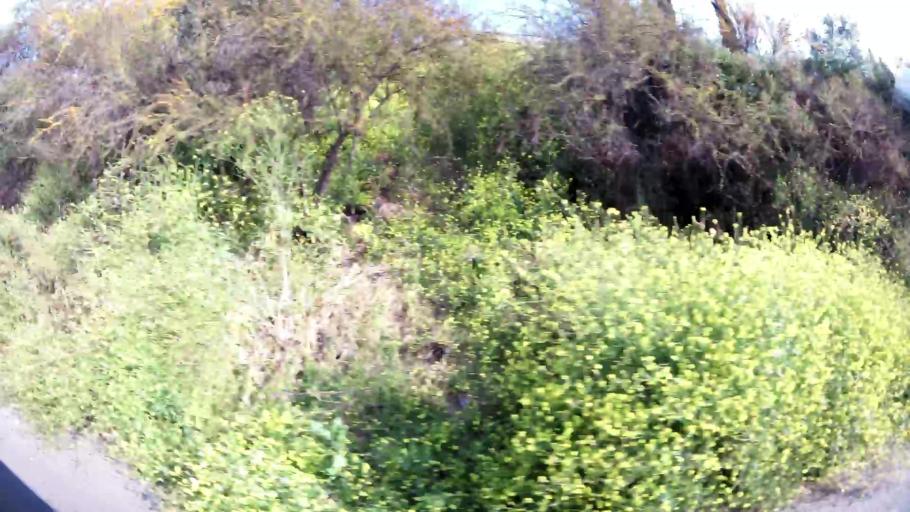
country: CL
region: Santiago Metropolitan
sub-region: Provincia de Santiago
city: Villa Presidente Frei, Nunoa, Santiago, Chile
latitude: -33.3677
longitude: -70.5292
